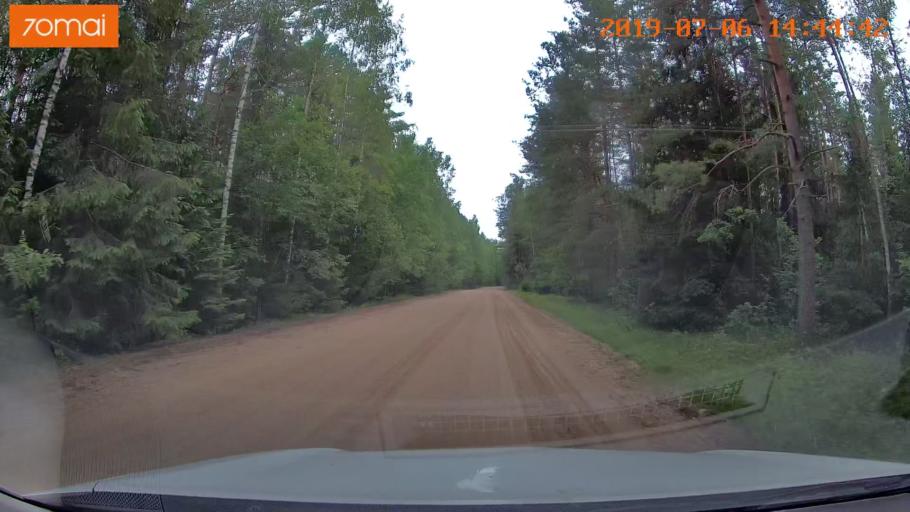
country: BY
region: Minsk
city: Ivyanyets
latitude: 53.9646
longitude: 26.6919
